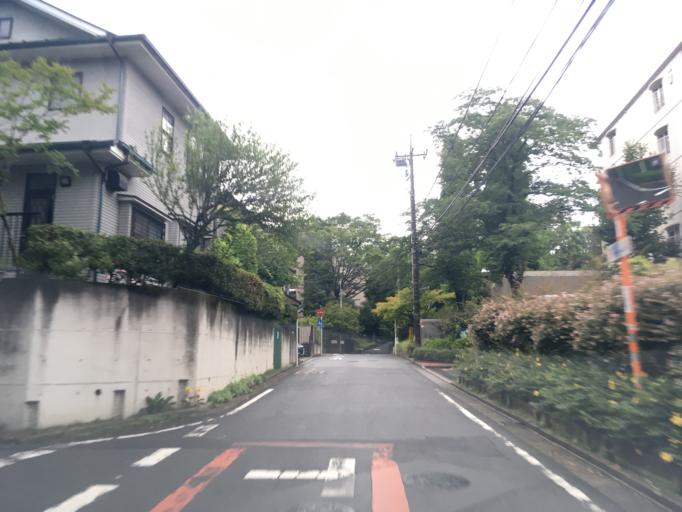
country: JP
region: Saitama
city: Tokorozawa
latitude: 35.7847
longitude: 139.4367
